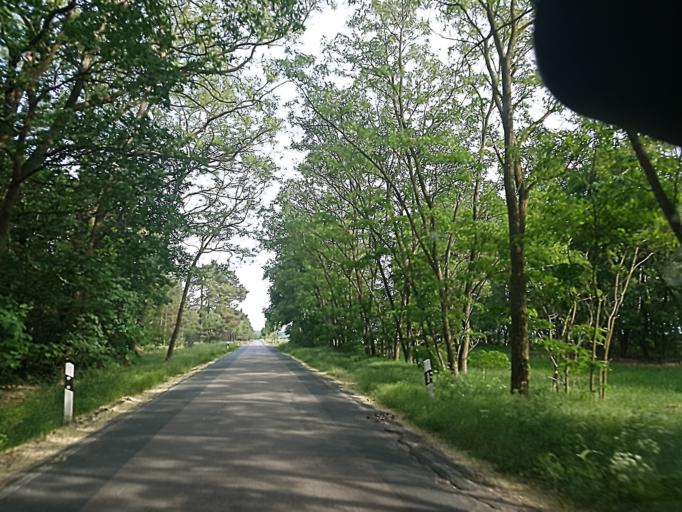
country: DE
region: Saxony-Anhalt
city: Seyda
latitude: 51.8394
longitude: 12.9286
